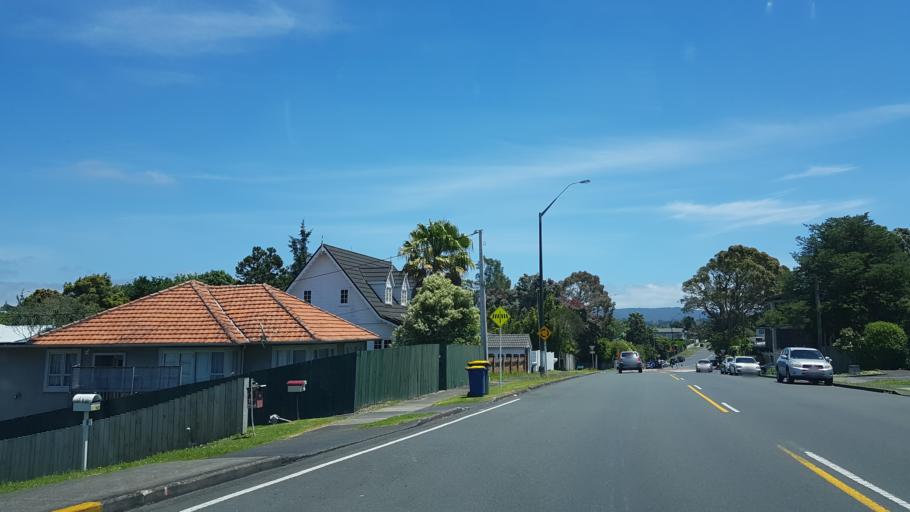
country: NZ
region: Auckland
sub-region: Auckland
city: Waitakere
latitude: -36.9122
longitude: 174.6539
